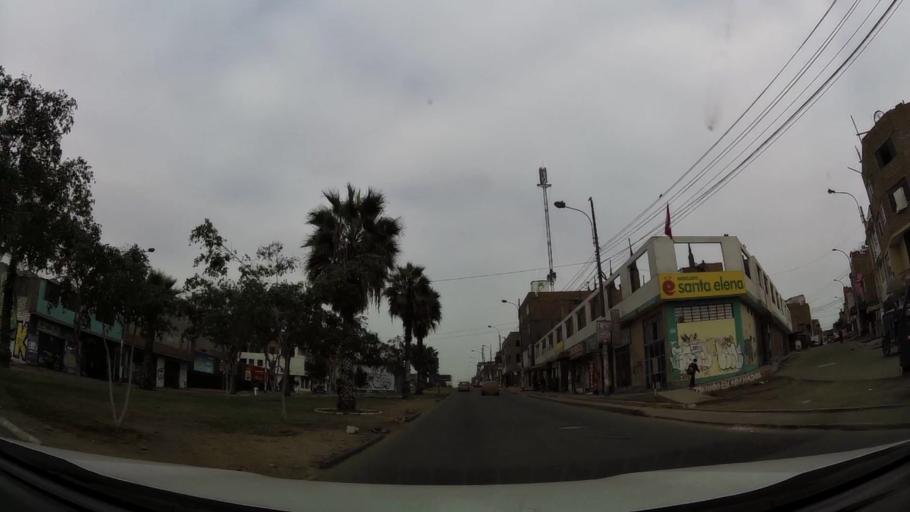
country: PE
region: Lima
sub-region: Lima
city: Independencia
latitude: -12.0174
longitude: -77.0774
